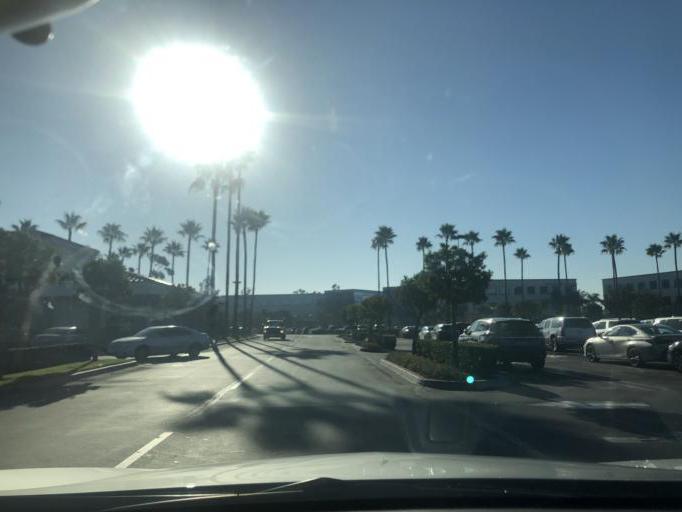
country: US
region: California
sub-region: Orange County
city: Foothill Ranch
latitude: 33.6769
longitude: -117.6667
